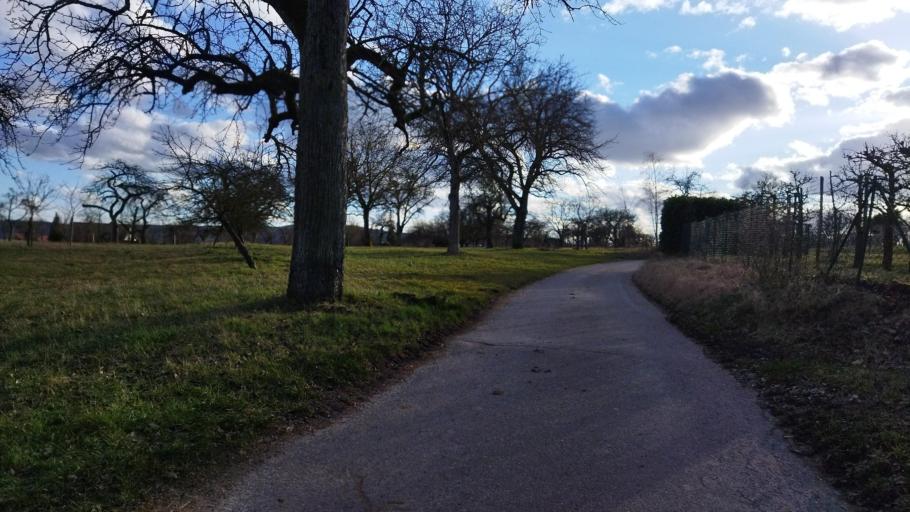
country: DE
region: Baden-Wuerttemberg
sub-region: Regierungsbezirk Stuttgart
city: Guglingen
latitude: 49.0733
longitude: 9.0019
